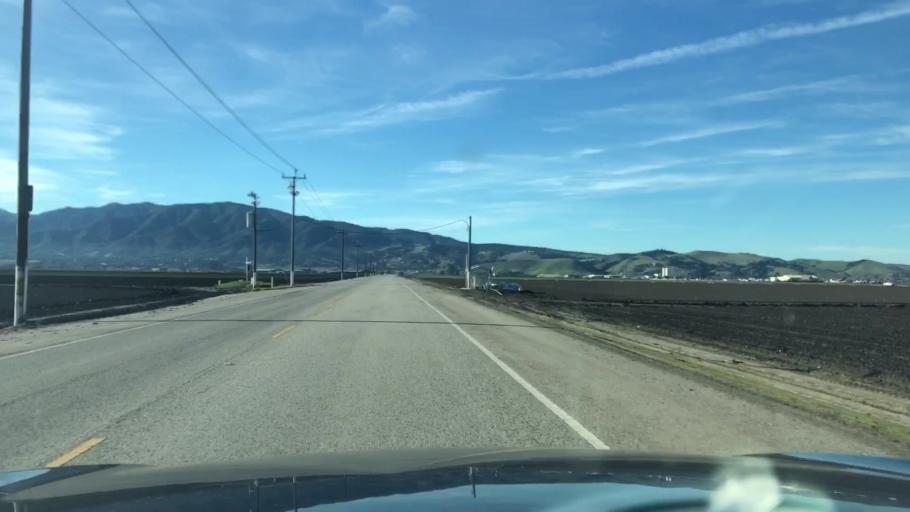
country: US
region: California
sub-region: Monterey County
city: Salinas
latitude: 36.6383
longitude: -121.6179
